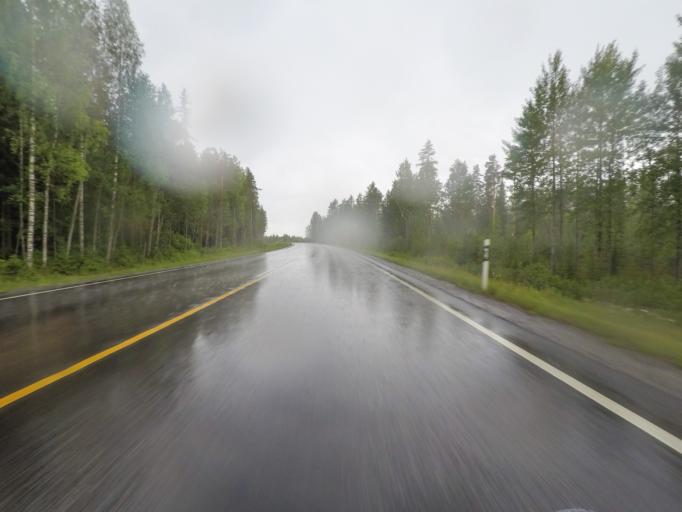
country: FI
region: Central Finland
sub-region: Jyvaeskylae
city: Hankasalmi
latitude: 62.3657
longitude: 26.5747
